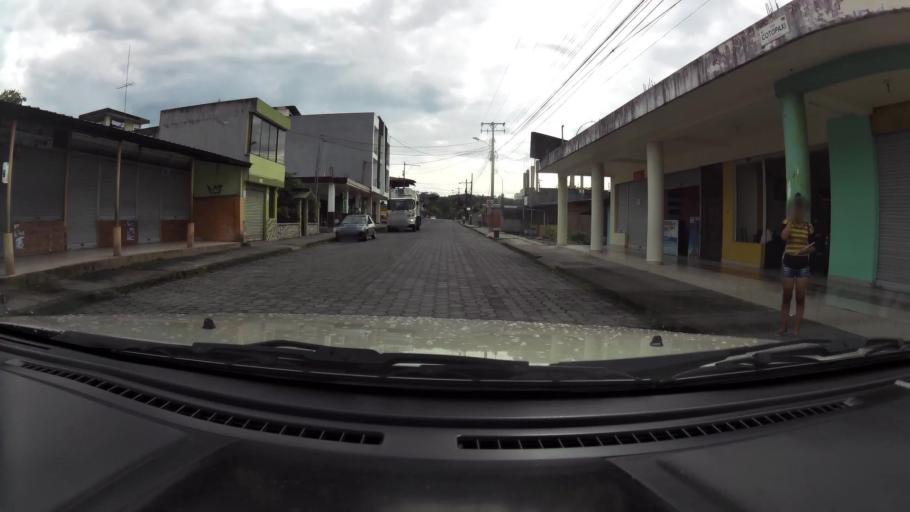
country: EC
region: Pastaza
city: Puyo
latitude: -1.4788
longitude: -78.0009
